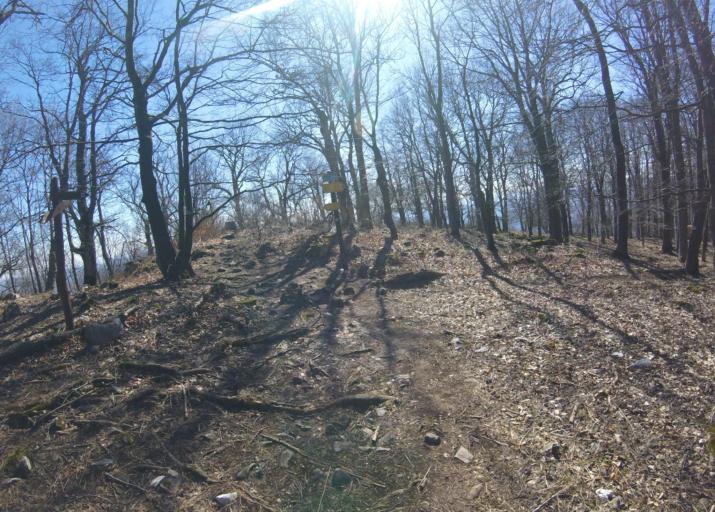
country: HU
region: Heves
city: Szilvasvarad
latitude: 48.0574
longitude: 20.4609
